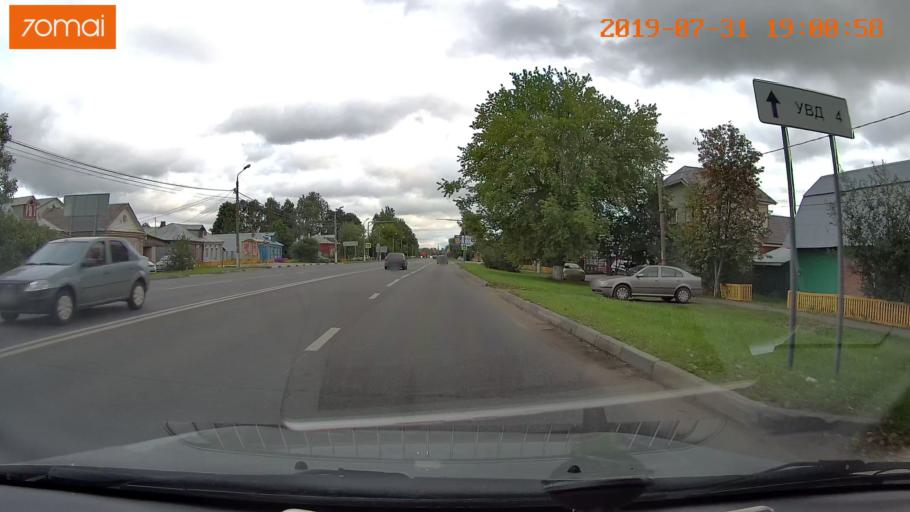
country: RU
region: Moskovskaya
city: Raduzhnyy
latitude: 55.1301
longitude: 38.7280
